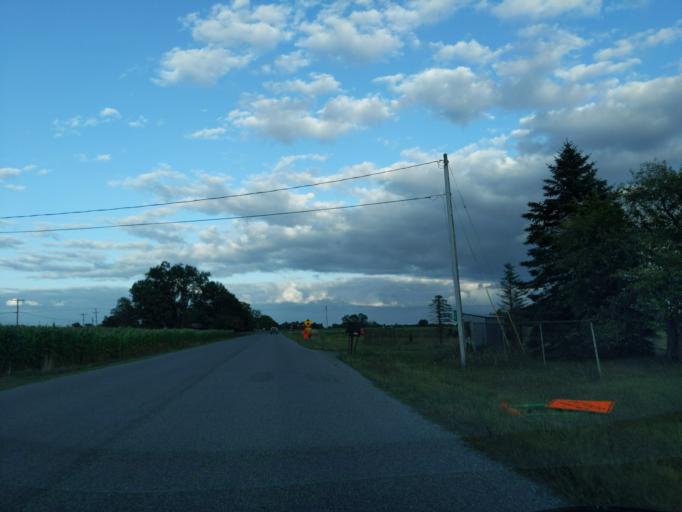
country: US
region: Michigan
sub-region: Ingham County
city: Holt
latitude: 42.5968
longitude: -84.5655
